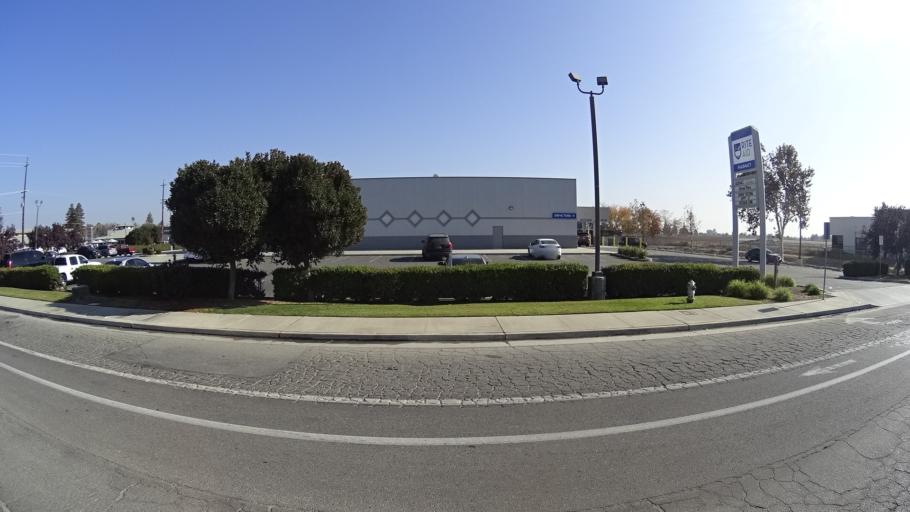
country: US
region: California
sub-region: Kern County
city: Greenfield
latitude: 35.2952
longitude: -119.0389
